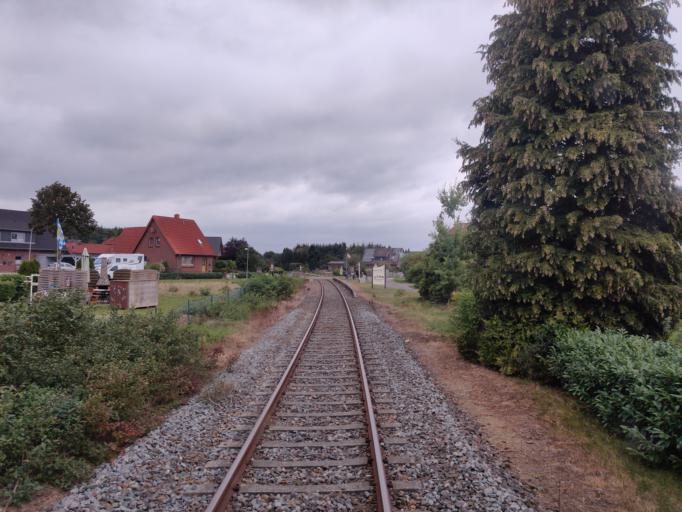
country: DE
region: Lower Saxony
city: Gnarrenburg
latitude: 53.3929
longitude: 9.0155
